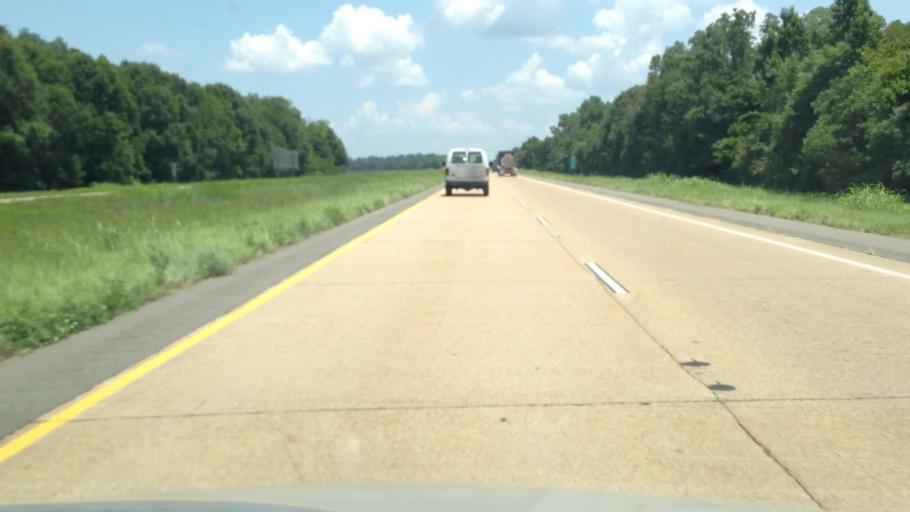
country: US
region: Louisiana
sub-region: Rapides Parish
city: Lecompte
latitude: 31.0067
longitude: -92.3564
